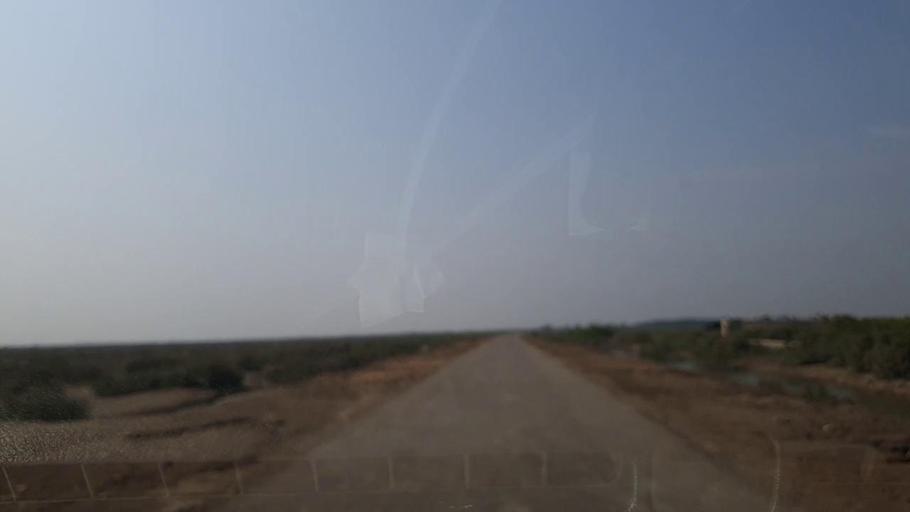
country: PK
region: Sindh
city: Gharo
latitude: 24.6733
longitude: 67.7008
